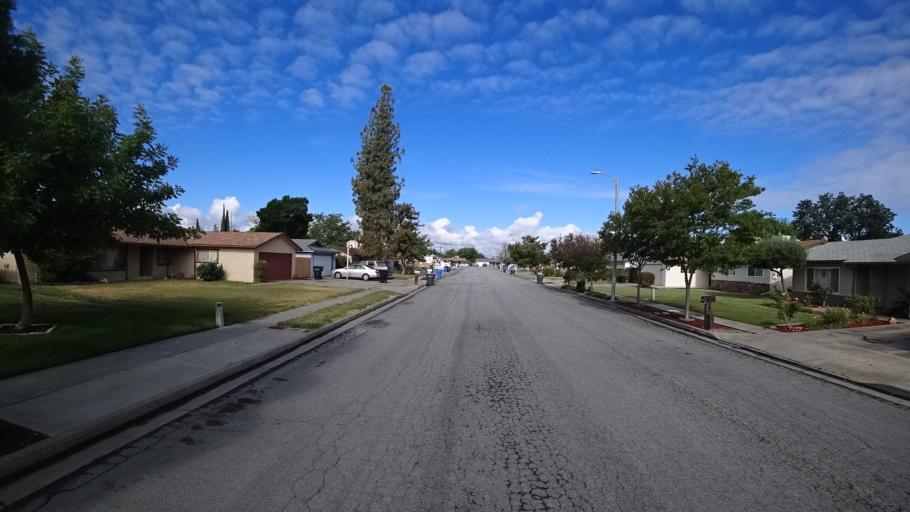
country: US
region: California
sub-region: Kings County
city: Lucerne
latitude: 36.3642
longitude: -119.6435
